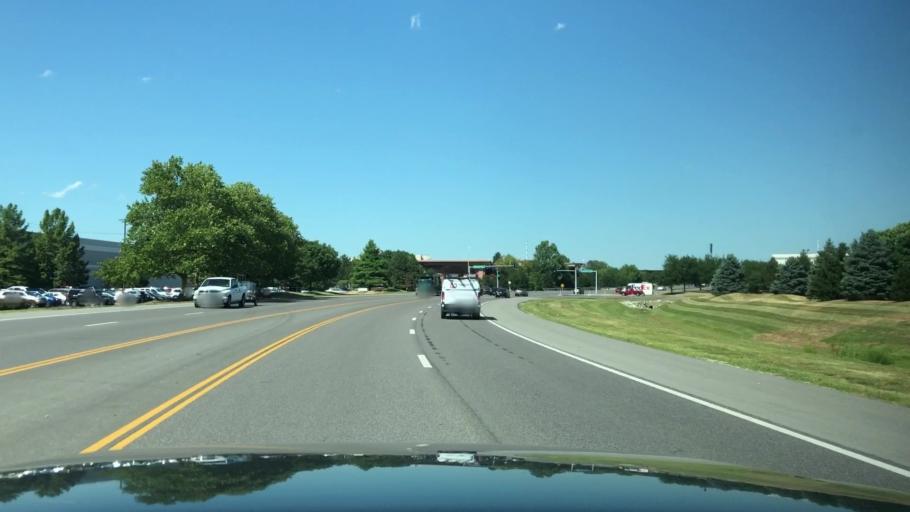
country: US
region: Missouri
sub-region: Saint Charles County
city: Saint Charles
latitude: 38.7864
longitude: -90.4590
